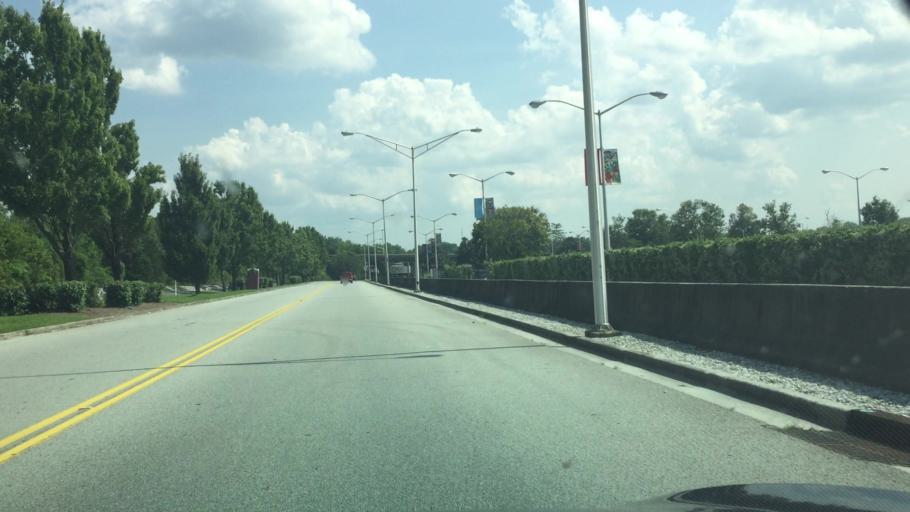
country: US
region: Tennessee
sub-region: Hamilton County
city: East Chattanooga
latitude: 35.0371
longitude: -85.1952
